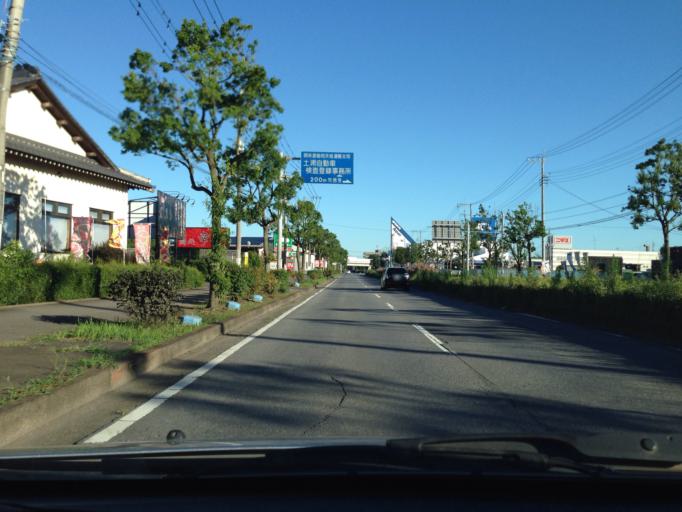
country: JP
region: Ibaraki
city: Naka
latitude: 36.0531
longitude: 140.1470
